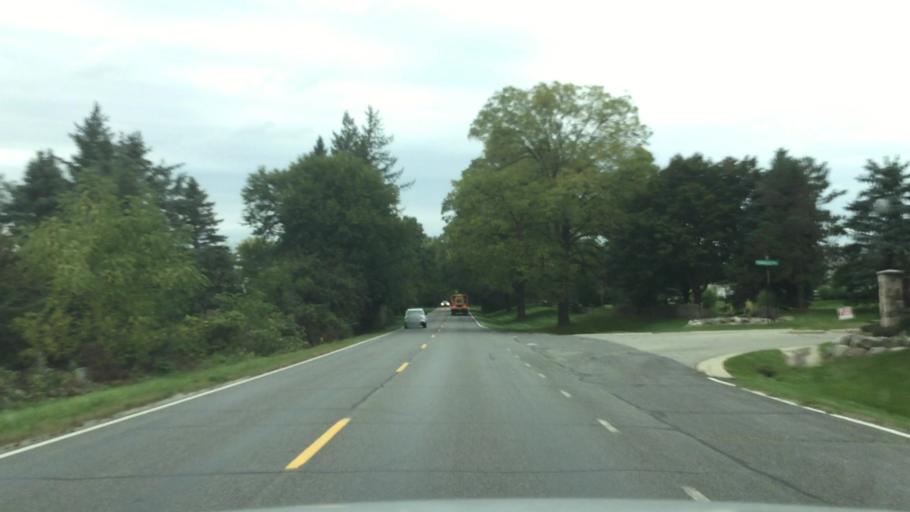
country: US
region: Michigan
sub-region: Livingston County
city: Brighton
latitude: 42.4904
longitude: -83.7678
